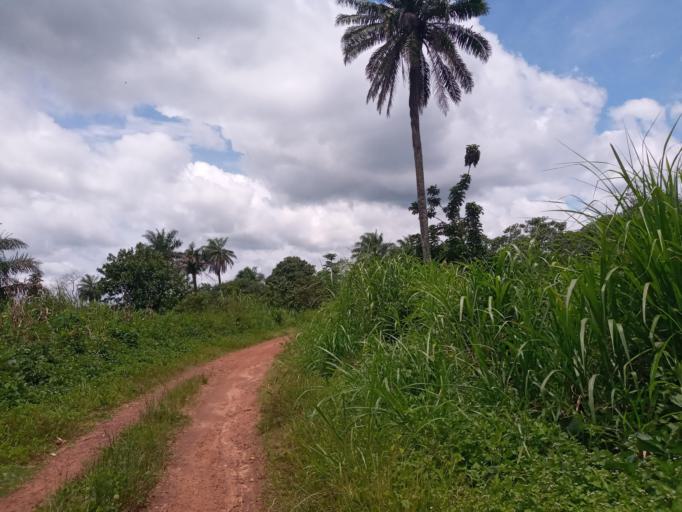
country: SL
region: Eastern Province
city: Koidu
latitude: 8.6448
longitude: -10.9089
